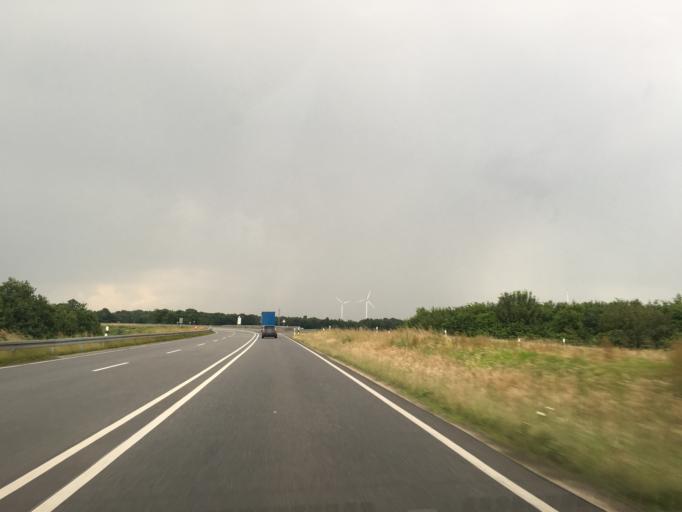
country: DE
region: North Rhine-Westphalia
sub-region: Regierungsbezirk Munster
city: Metelen
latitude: 52.1717
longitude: 7.2595
